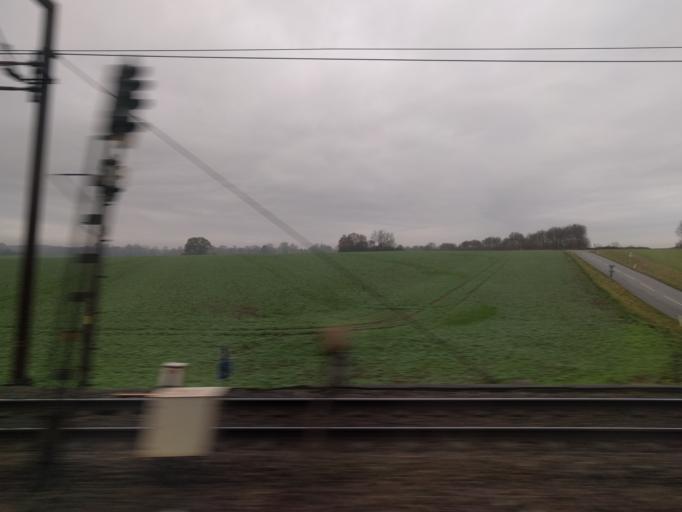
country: DK
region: Zealand
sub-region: Koge Kommune
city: Borup
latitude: 55.4911
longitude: 11.9712
